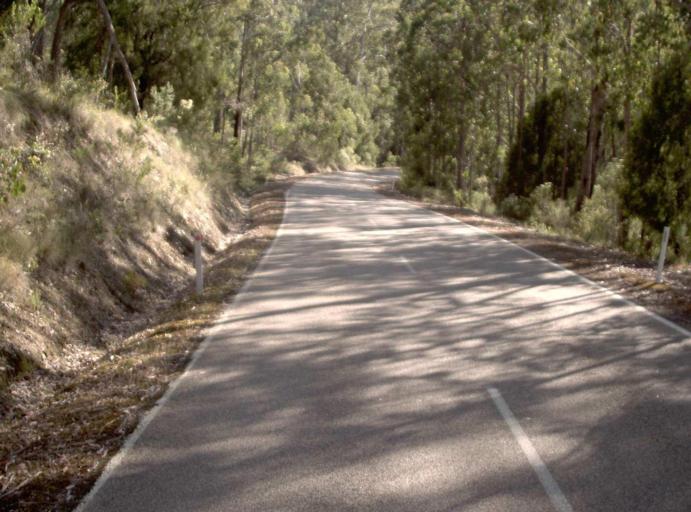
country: AU
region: Victoria
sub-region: East Gippsland
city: Lakes Entrance
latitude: -37.5659
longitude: 148.5506
